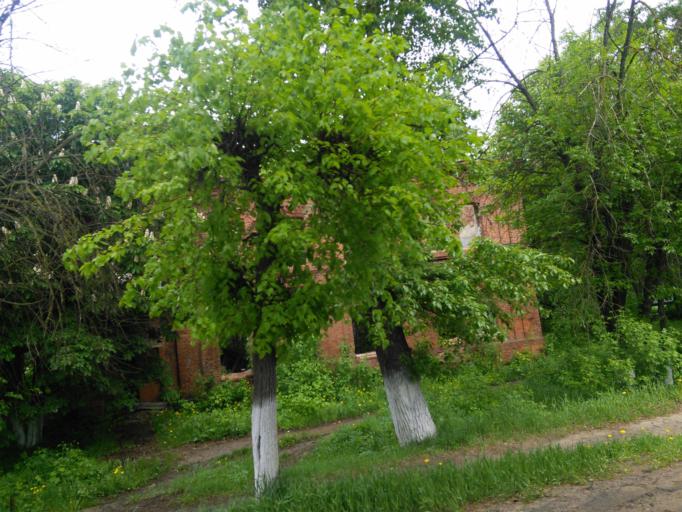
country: RU
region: Moskovskaya
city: Serpukhov
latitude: 54.9272
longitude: 37.3715
